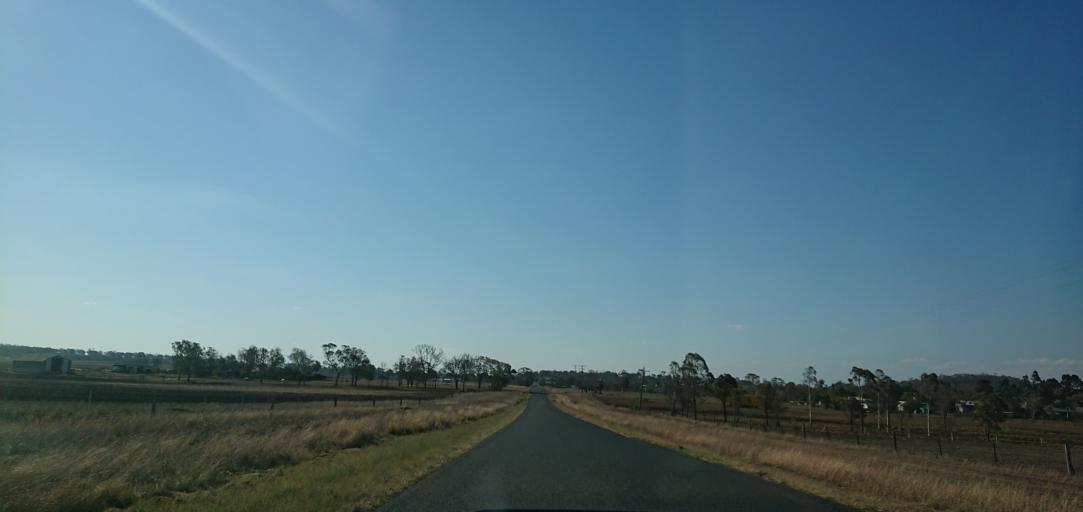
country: AU
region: Queensland
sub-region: Toowoomba
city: Westbrook
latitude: -27.6943
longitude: 151.7159
